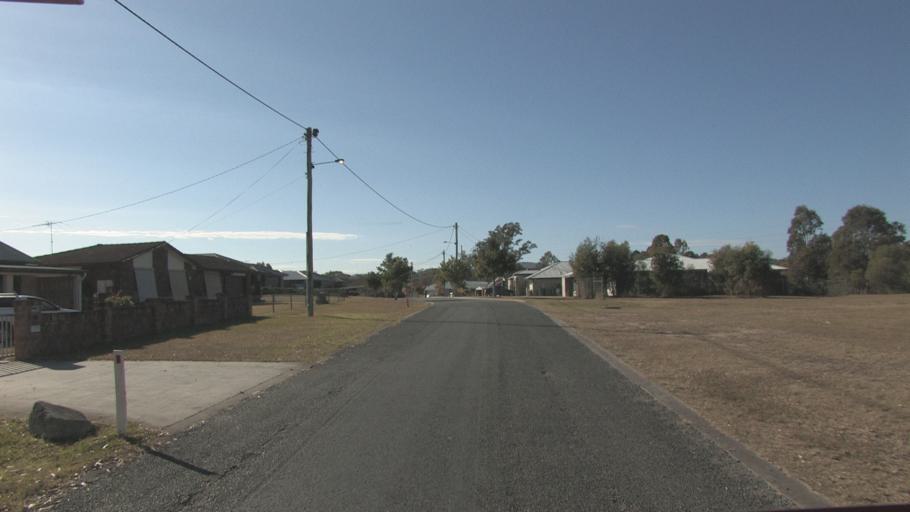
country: AU
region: Queensland
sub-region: Logan
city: Cedar Vale
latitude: -27.8295
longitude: 153.0339
